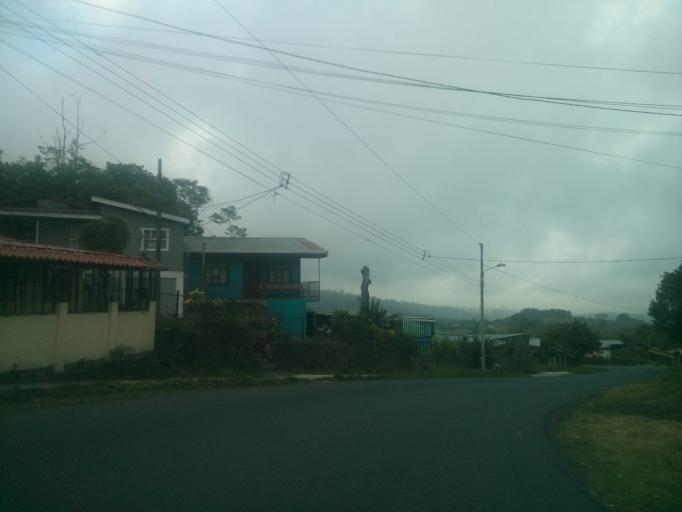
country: CR
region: Cartago
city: Cot
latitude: 9.8883
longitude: -83.8046
